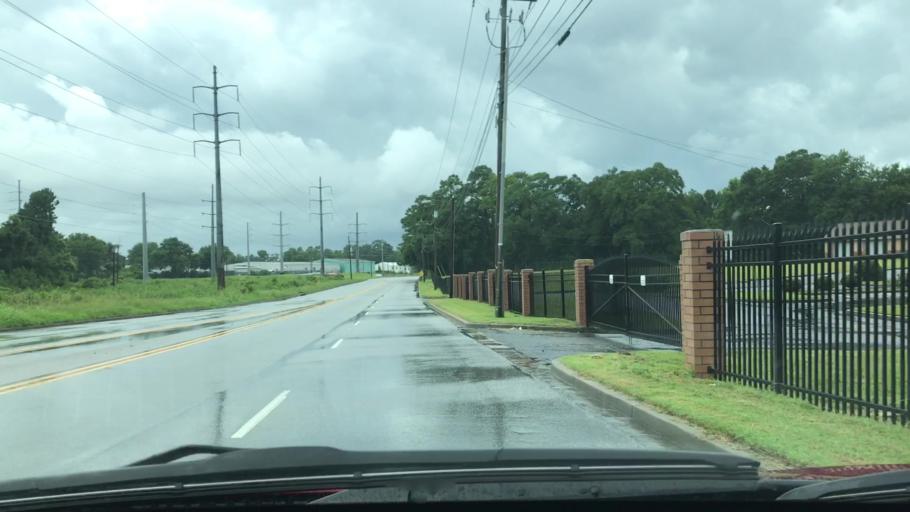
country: US
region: South Carolina
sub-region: Charleston County
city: North Charleston
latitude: 32.8470
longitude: -79.9974
